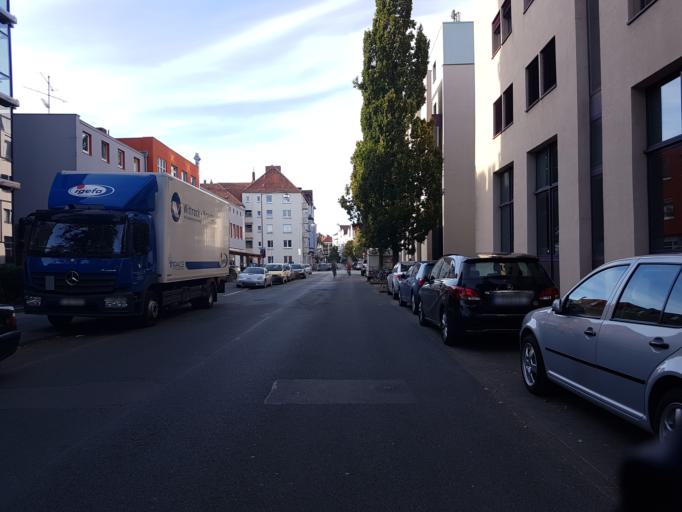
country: DE
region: Lower Saxony
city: Hannover
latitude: 52.3871
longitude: 9.7417
